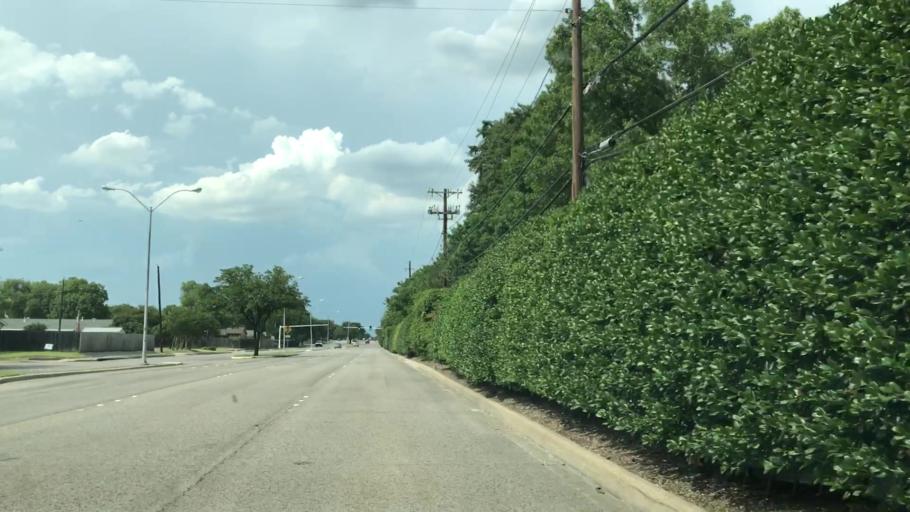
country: US
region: Texas
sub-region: Dallas County
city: Carrollton
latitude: 32.9366
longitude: -96.8730
